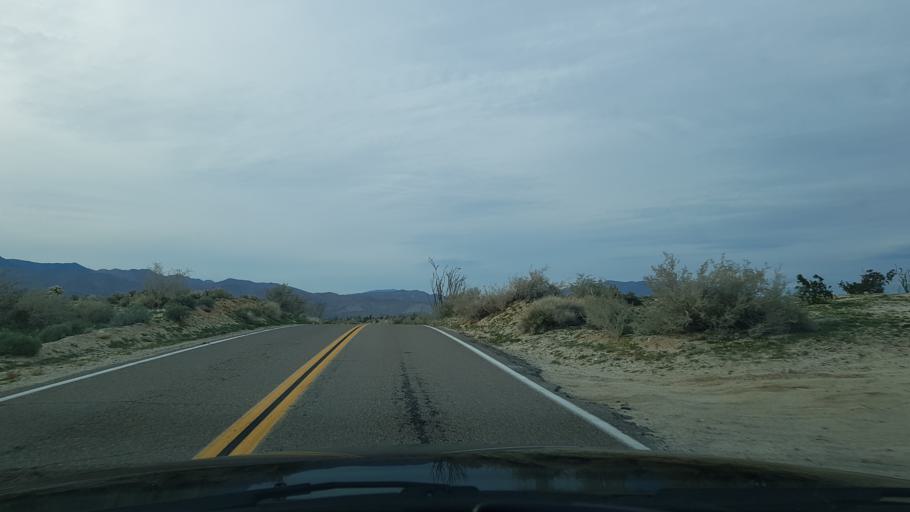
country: MX
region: Baja California
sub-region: Tecate
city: Cereso del Hongo
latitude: 32.8265
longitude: -116.1654
